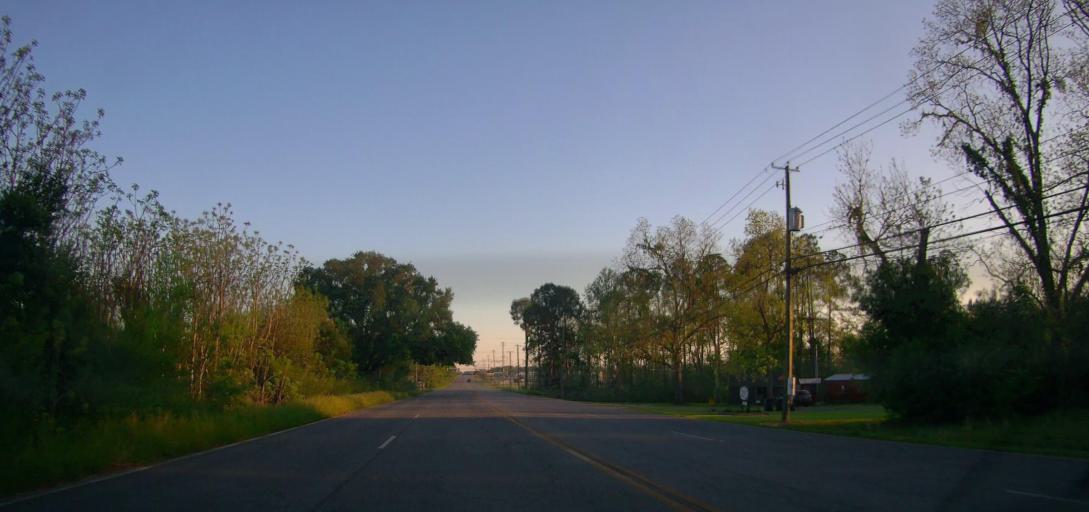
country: US
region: Georgia
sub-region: Ben Hill County
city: Fitzgerald
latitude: 31.6944
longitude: -83.2610
